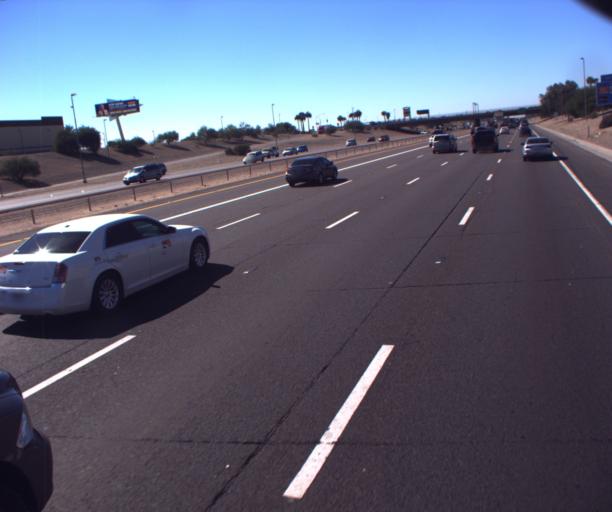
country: US
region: Arizona
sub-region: Maricopa County
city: Tolleson
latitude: 33.4630
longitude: -112.1994
